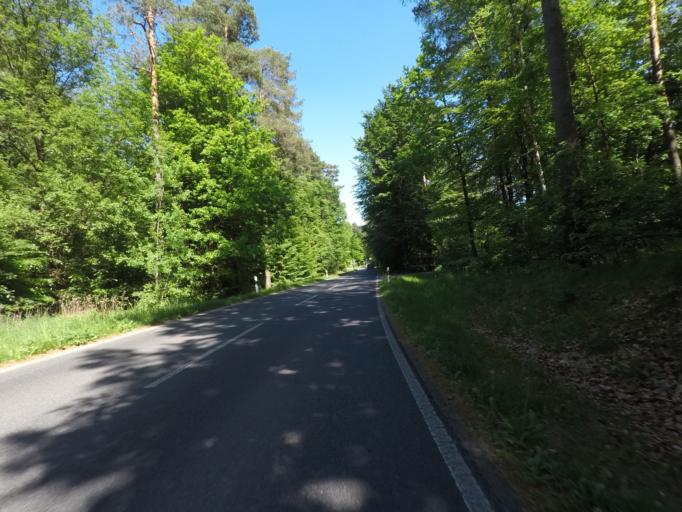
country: DE
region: Brandenburg
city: Eberswalde
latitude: 52.8244
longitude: 13.7768
